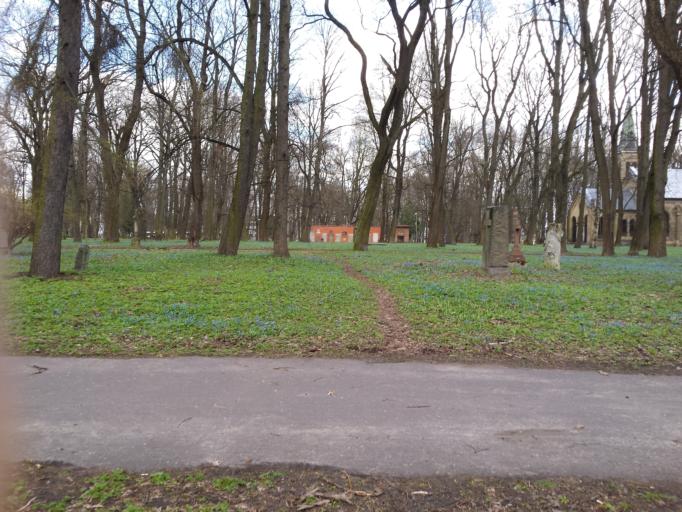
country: LV
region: Riga
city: Riga
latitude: 56.9711
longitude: 24.1446
